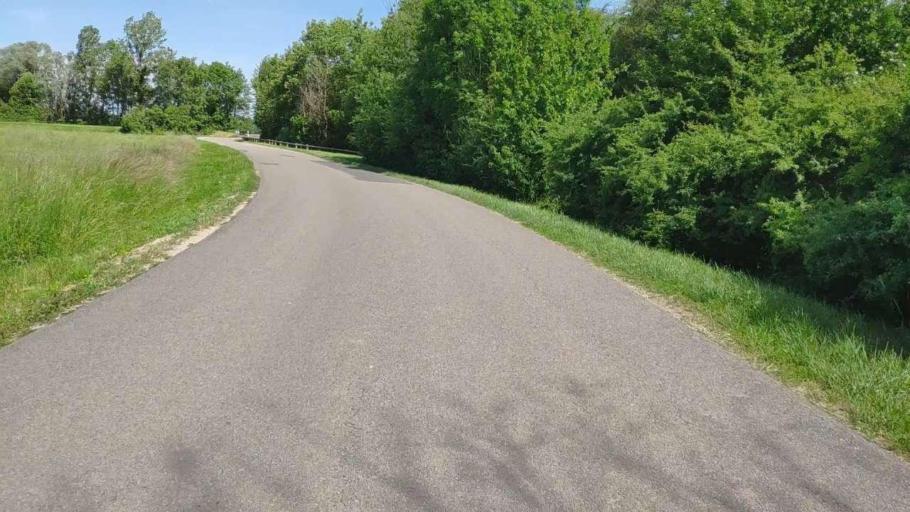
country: FR
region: Franche-Comte
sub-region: Departement du Jura
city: Bletterans
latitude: 46.7246
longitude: 5.4447
